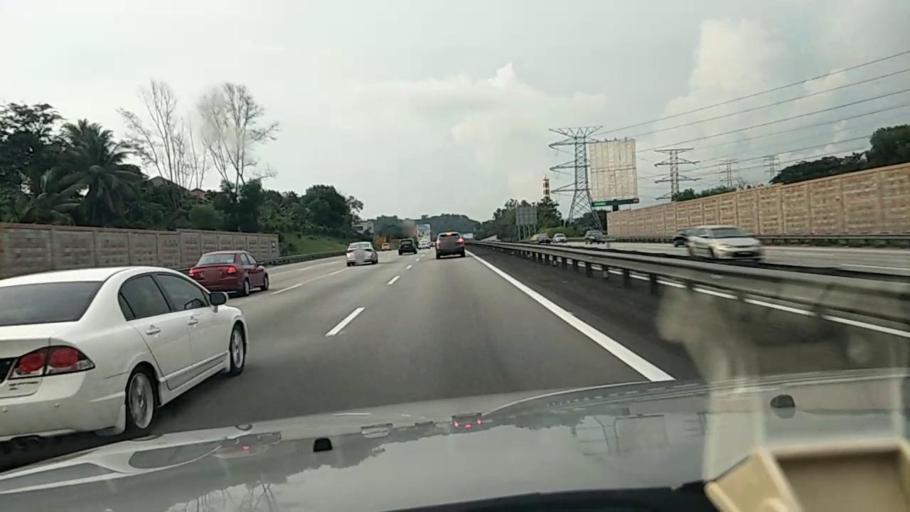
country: MY
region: Selangor
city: Kuang
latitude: 3.2407
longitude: 101.5660
